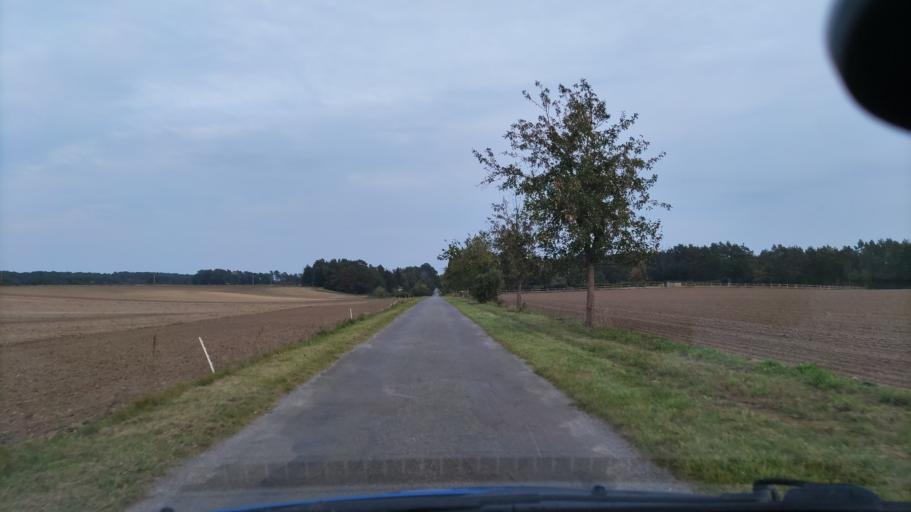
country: DE
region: Lower Saxony
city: Karwitz
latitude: 53.0911
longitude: 10.9886
